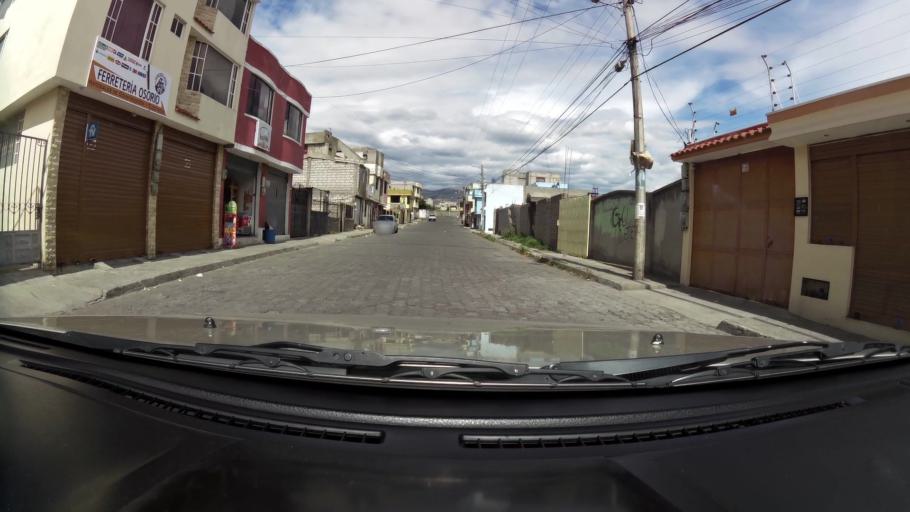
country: EC
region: Cotopaxi
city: Latacunga
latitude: -0.9259
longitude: -78.6066
